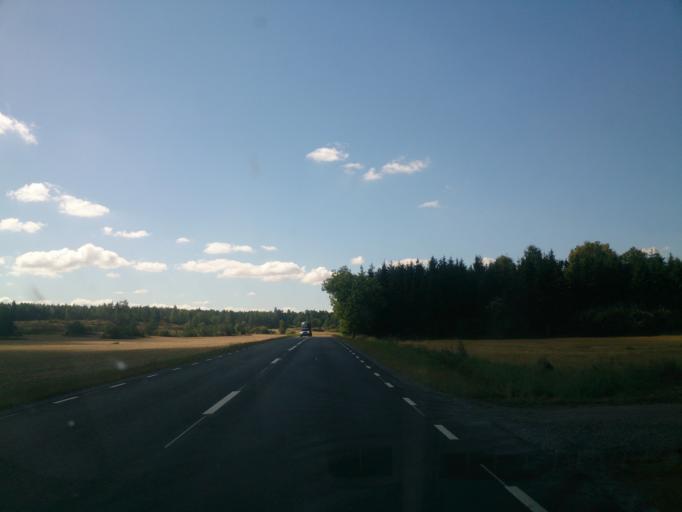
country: SE
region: OEstergoetland
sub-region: Norrkopings Kommun
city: Krokek
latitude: 58.5790
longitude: 16.5263
